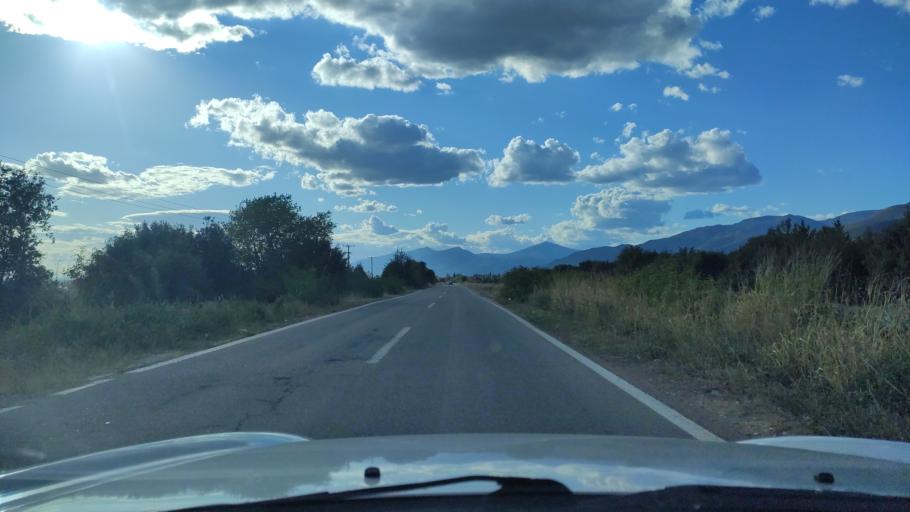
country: GR
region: East Macedonia and Thrace
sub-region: Nomos Xanthis
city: Selero
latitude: 41.1213
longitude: 25.0776
